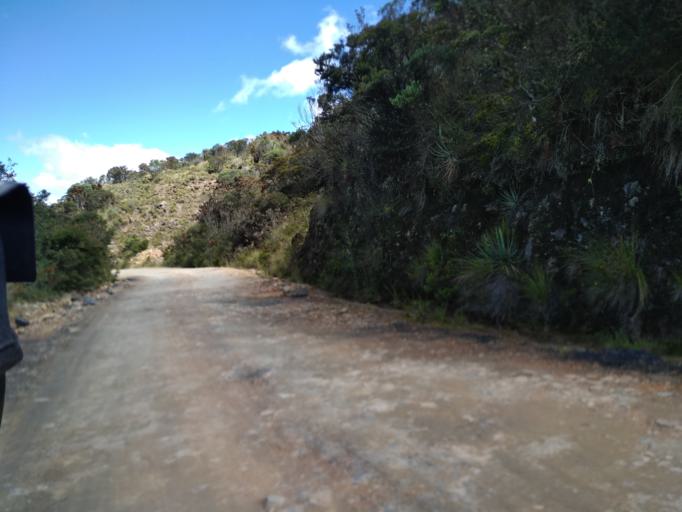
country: CO
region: Boyaca
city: Duitama
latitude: 5.9371
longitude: -73.1023
